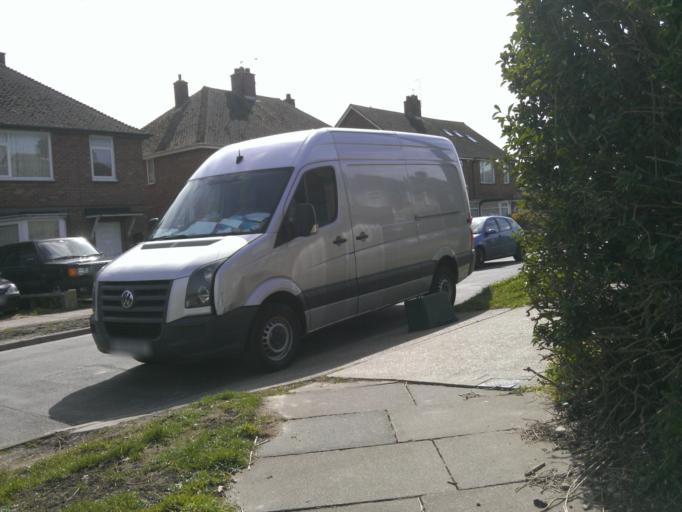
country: GB
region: England
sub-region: Essex
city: Clacton-on-Sea
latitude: 51.8025
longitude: 1.1569
